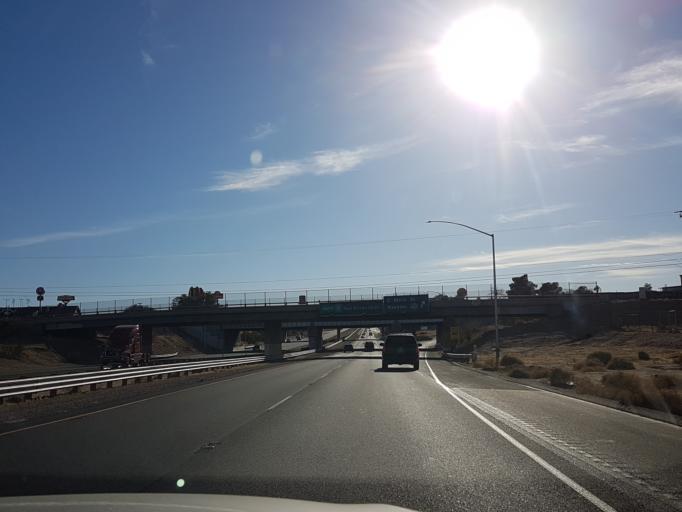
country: US
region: California
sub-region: San Bernardino County
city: Barstow
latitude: 34.8940
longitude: -116.9977
